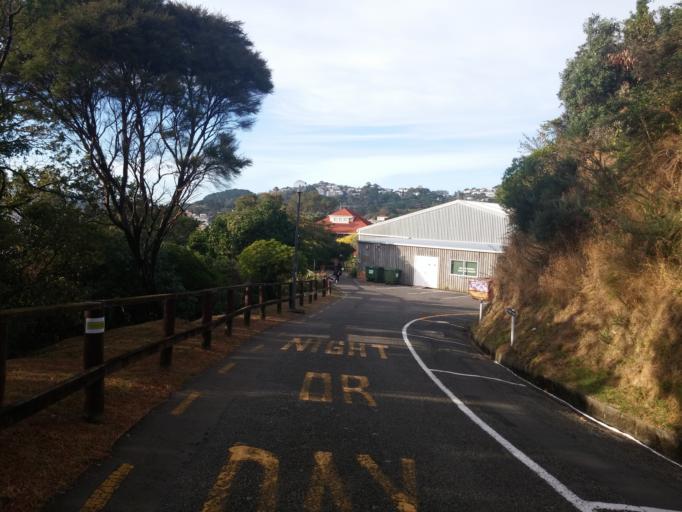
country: NZ
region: Wellington
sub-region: Wellington City
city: Wellington
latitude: -41.2912
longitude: 174.7692
